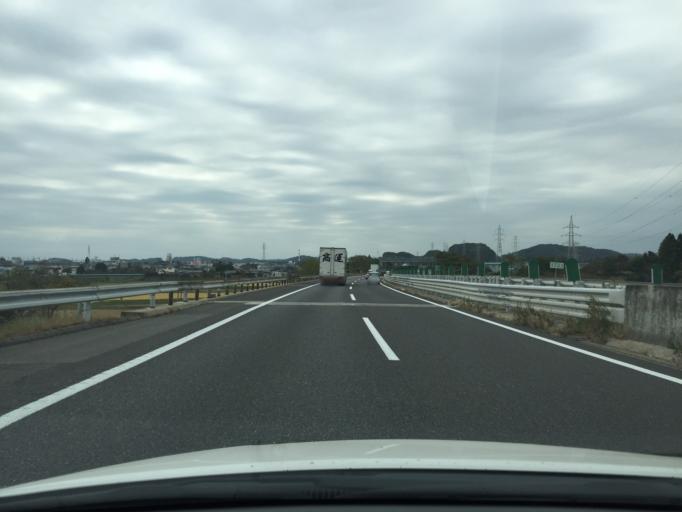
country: JP
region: Tochigi
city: Kuroiso
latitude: 37.1400
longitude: 140.1972
